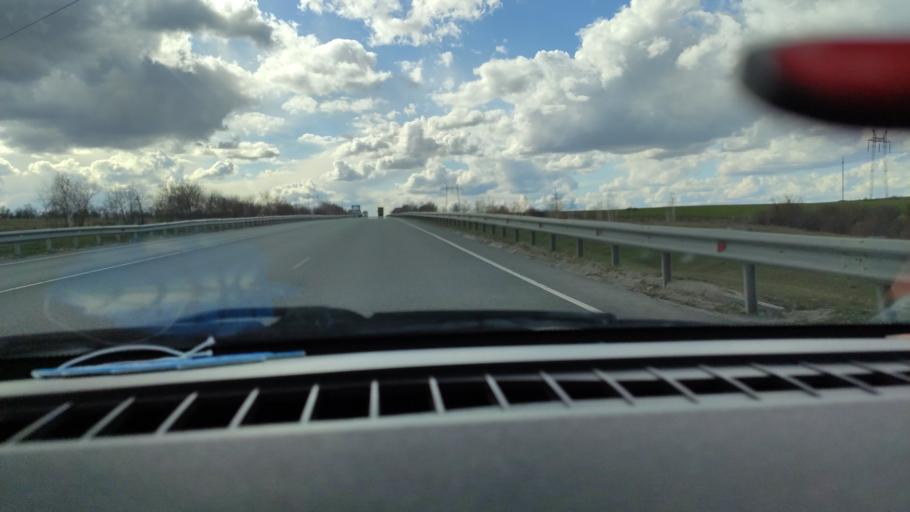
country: RU
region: Saratov
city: Tersa
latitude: 52.1004
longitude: 47.5142
